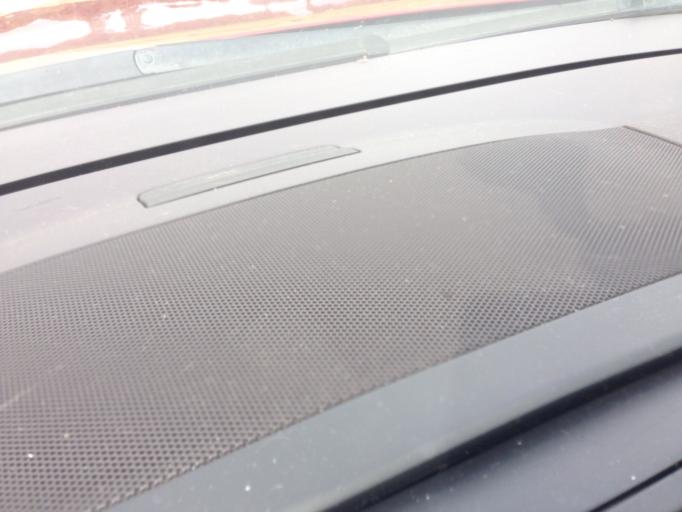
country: US
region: Montana
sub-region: Sweet Grass County
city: Big Timber
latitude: 45.7836
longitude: -109.8327
